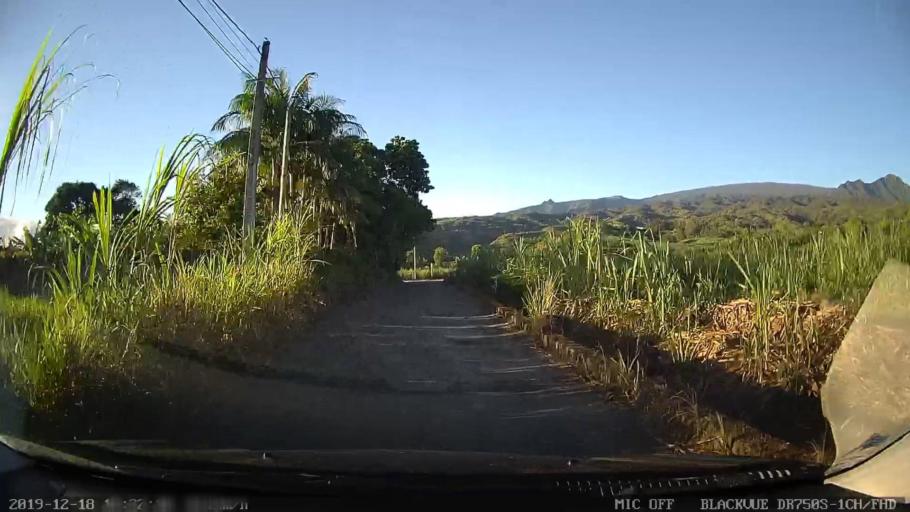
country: RE
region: Reunion
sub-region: Reunion
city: Bras-Panon
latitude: -20.9979
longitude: 55.6622
